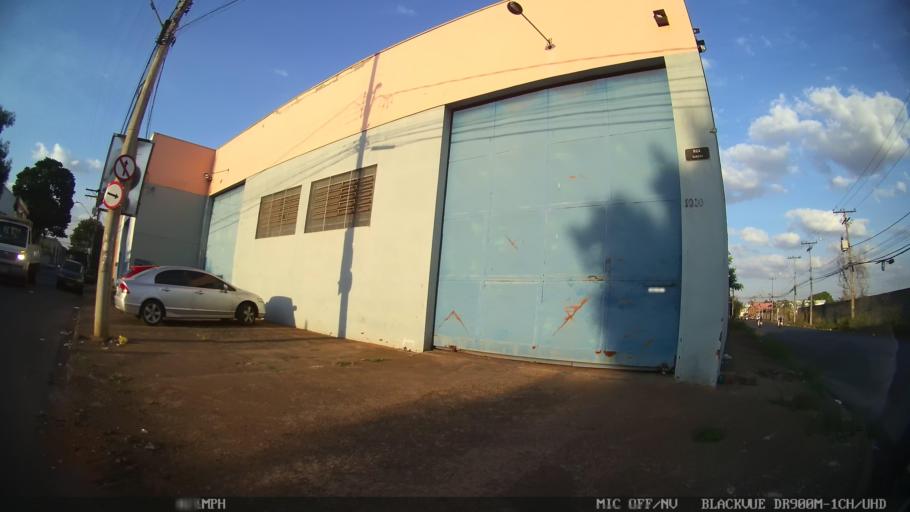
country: BR
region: Sao Paulo
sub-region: Ribeirao Preto
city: Ribeirao Preto
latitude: -21.1425
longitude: -47.7899
